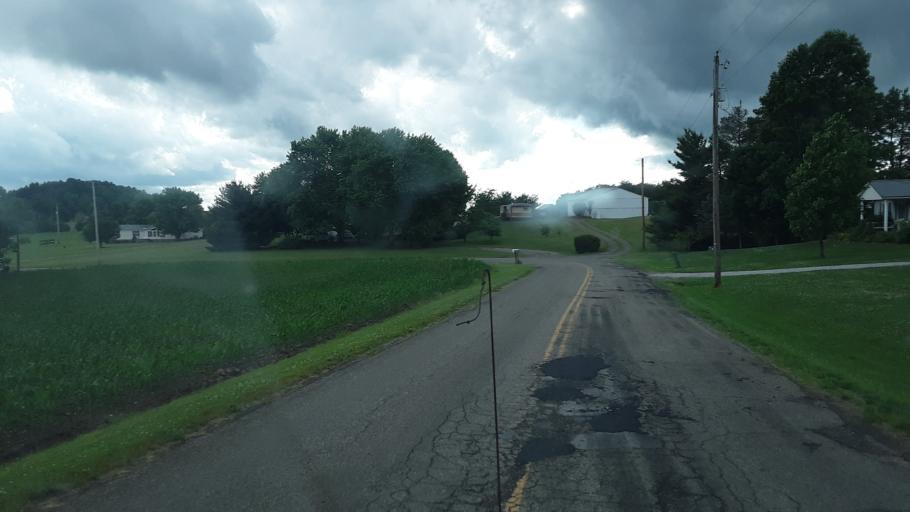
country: US
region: Ohio
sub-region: Carroll County
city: Carrollton
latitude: 40.5603
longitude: -81.0778
